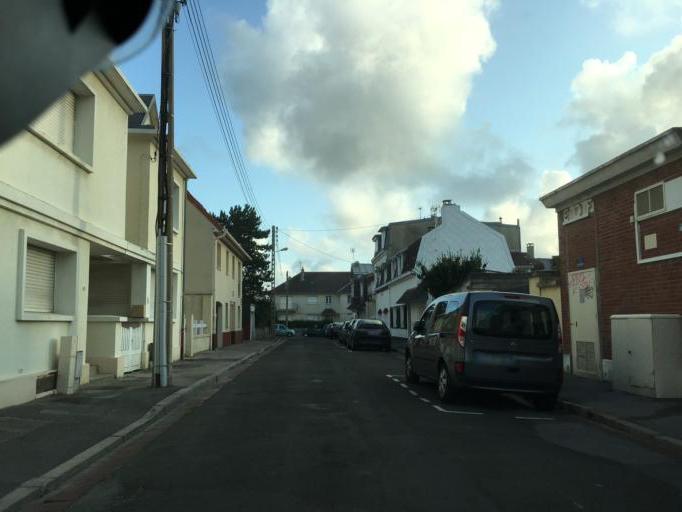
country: FR
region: Nord-Pas-de-Calais
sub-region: Departement du Pas-de-Calais
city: Berck-Plage
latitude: 50.4068
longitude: 1.5629
